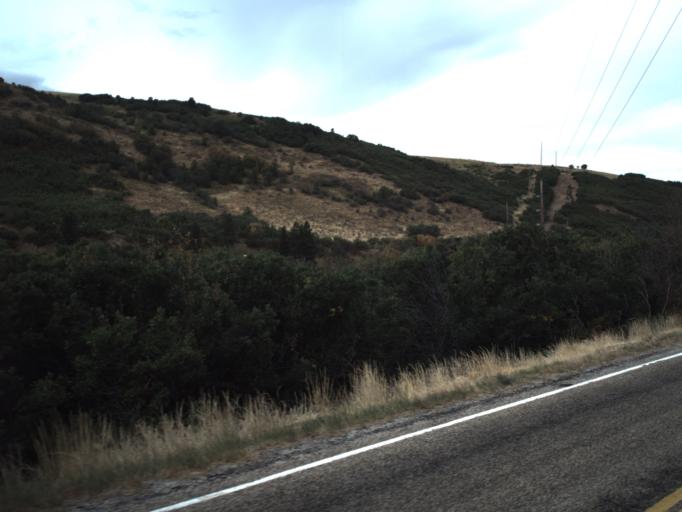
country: US
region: Utah
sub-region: Morgan County
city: Morgan
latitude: 40.9445
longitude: -111.6496
